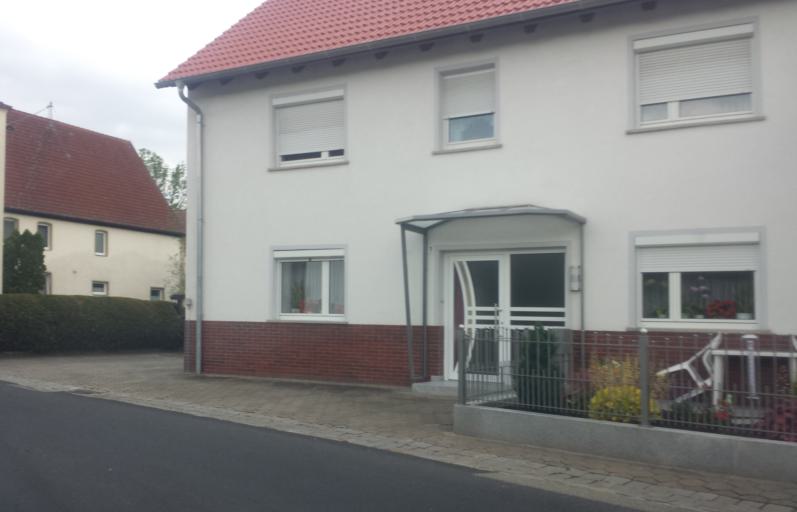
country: DE
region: Bavaria
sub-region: Regierungsbezirk Mittelfranken
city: Munchsteinach
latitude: 49.6593
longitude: 10.5717
